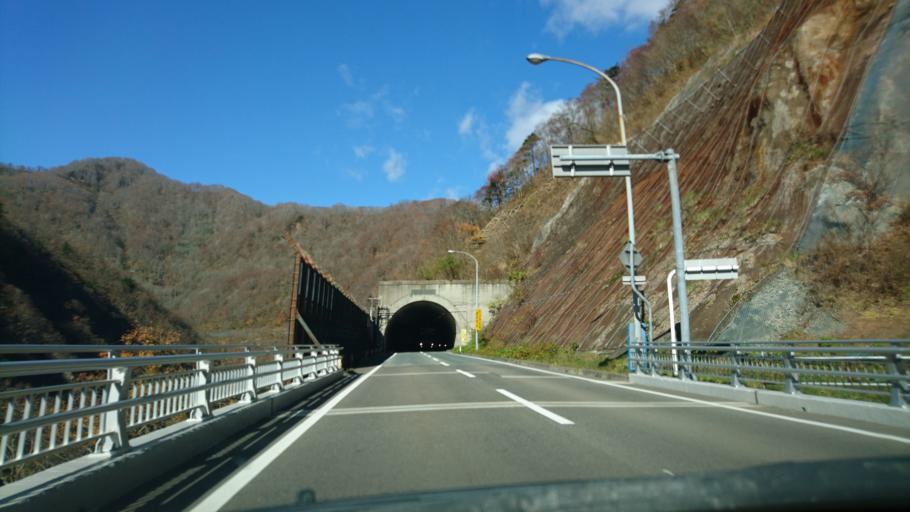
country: JP
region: Iwate
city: Kitakami
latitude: 39.3024
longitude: 140.8935
